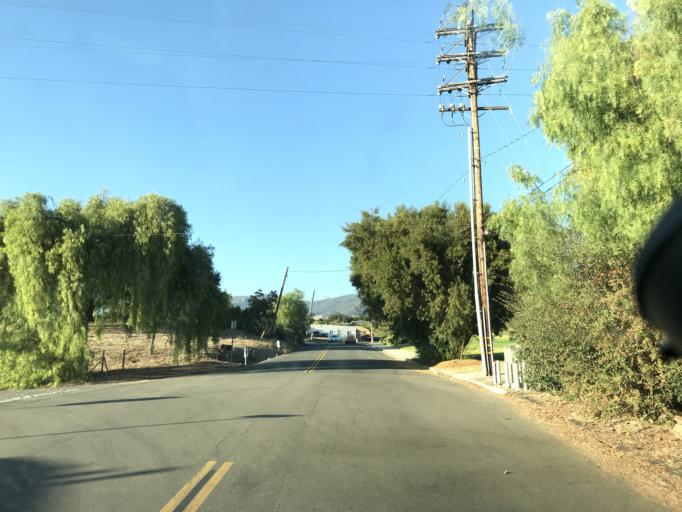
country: US
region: California
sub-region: Santa Barbara County
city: Mission Canyon
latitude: 34.4550
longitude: -119.7598
